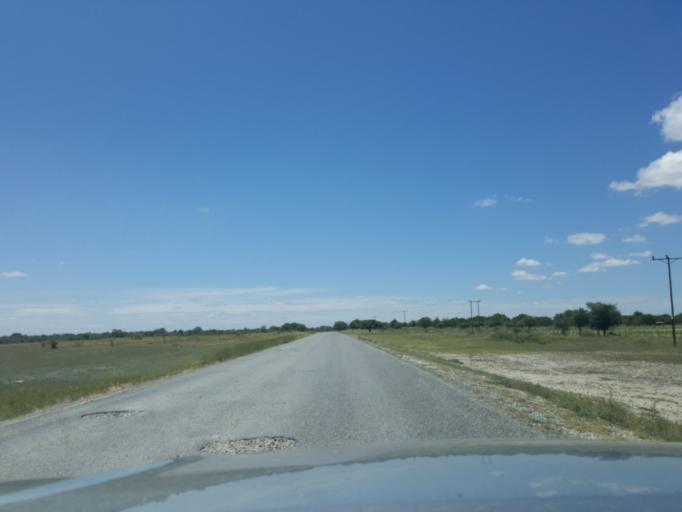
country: BW
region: Central
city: Nata
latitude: -20.1590
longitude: 25.8464
